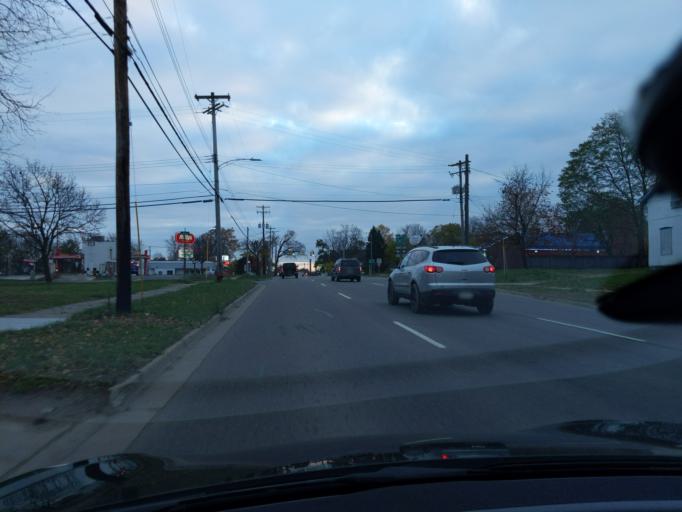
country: US
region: Michigan
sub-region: Ingham County
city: Lansing
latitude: 42.7448
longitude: -84.5465
